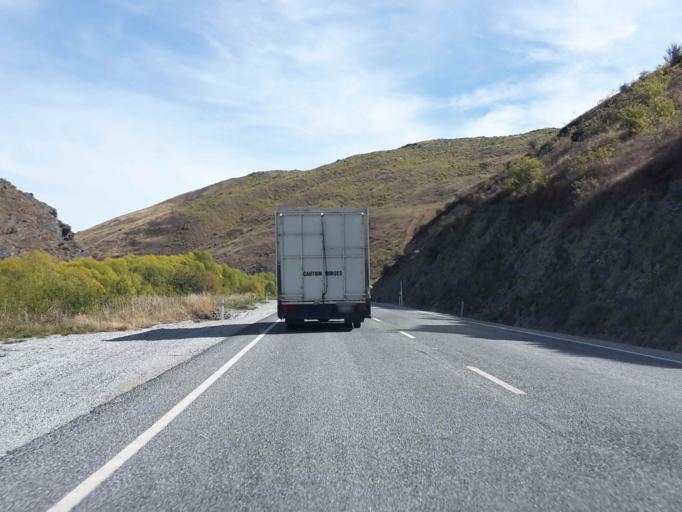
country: NZ
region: Otago
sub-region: Queenstown-Lakes District
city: Wanaka
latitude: -44.6959
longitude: 169.4933
